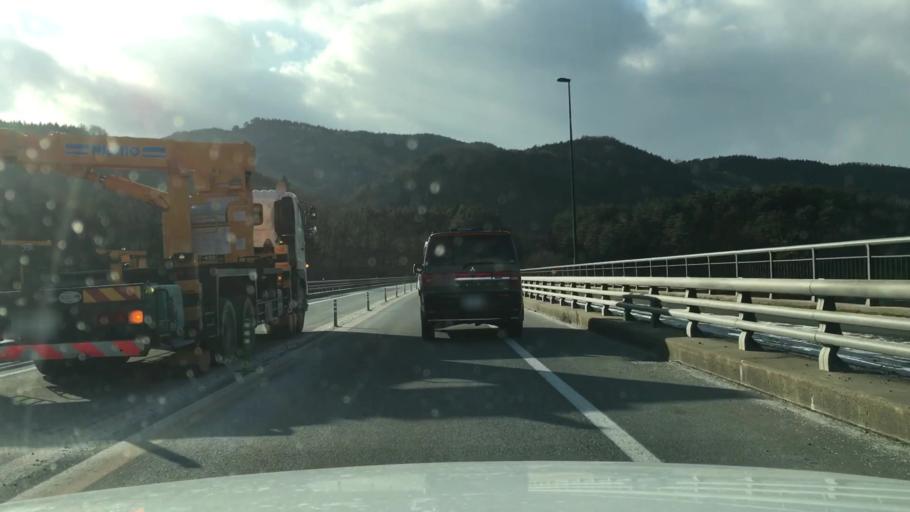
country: JP
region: Iwate
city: Morioka-shi
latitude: 39.6675
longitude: 141.2464
